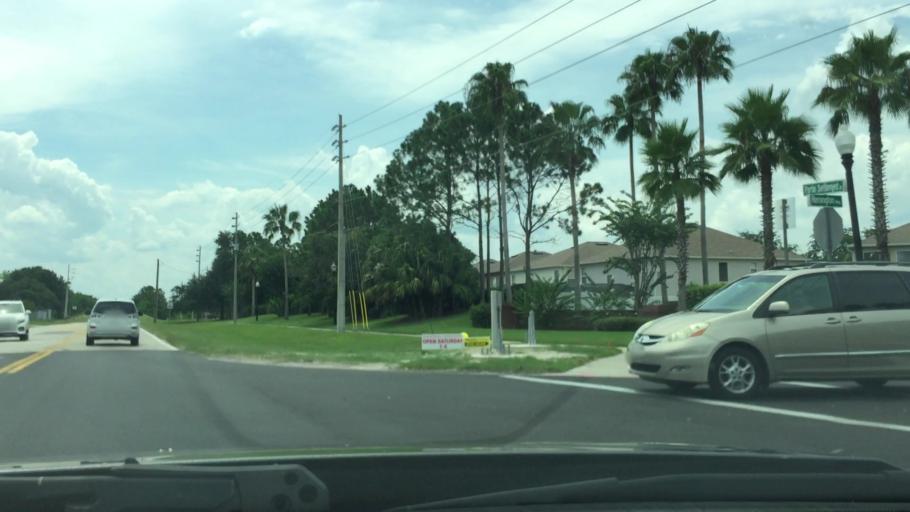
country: US
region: Florida
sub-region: Osceola County
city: Saint Cloud
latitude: 28.2791
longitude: -81.3326
